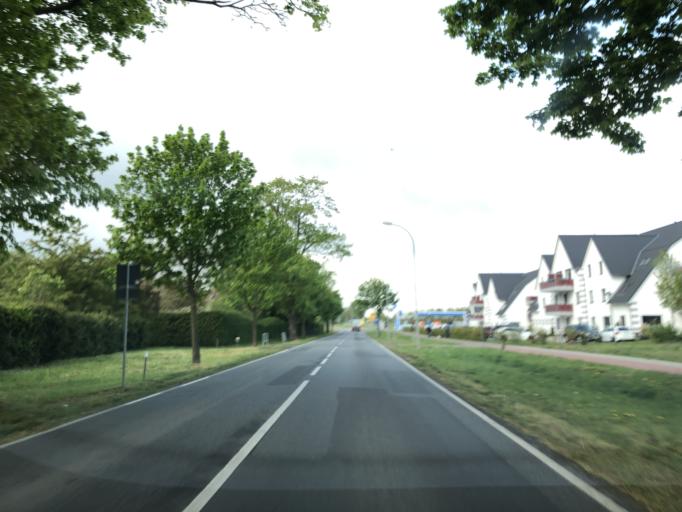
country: DE
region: Mecklenburg-Vorpommern
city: Guestrow
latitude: 53.7737
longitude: 12.1690
